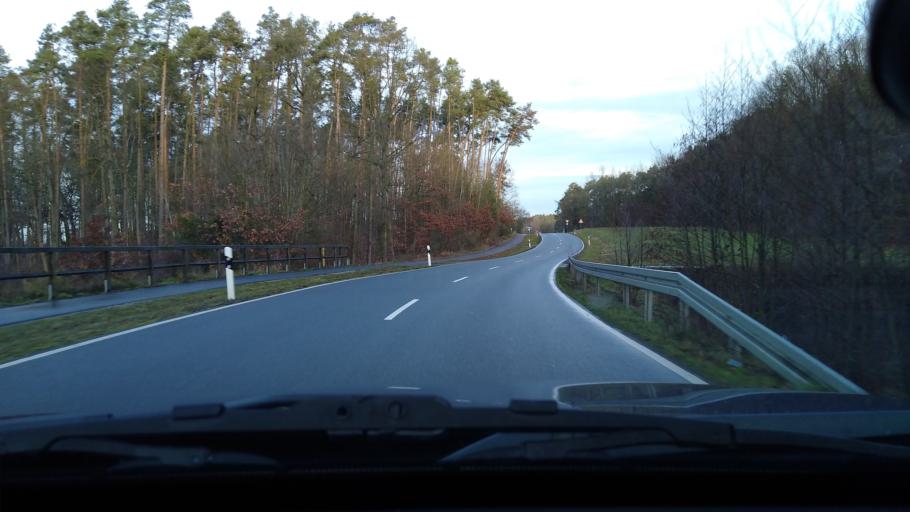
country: DE
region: Bavaria
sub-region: Regierungsbezirk Mittelfranken
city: Hemhofen
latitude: 49.6978
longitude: 10.9326
